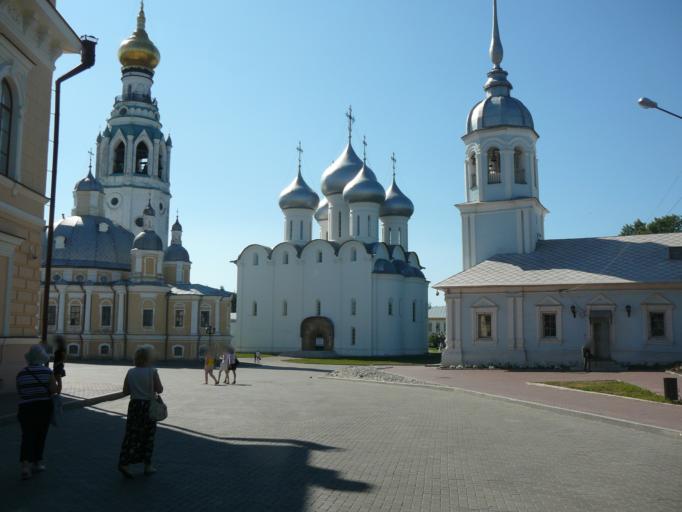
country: RU
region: Vologda
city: Vologda
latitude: 59.2242
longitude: 39.8846
